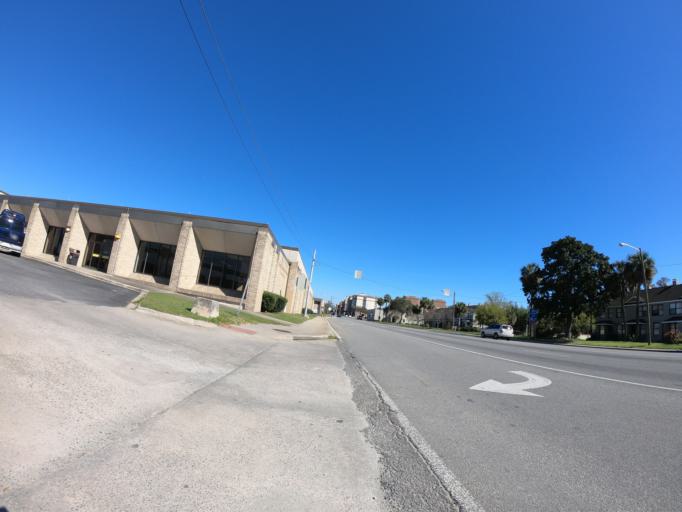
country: US
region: Georgia
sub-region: Chatham County
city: Savannah
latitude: 32.0832
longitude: -81.0993
